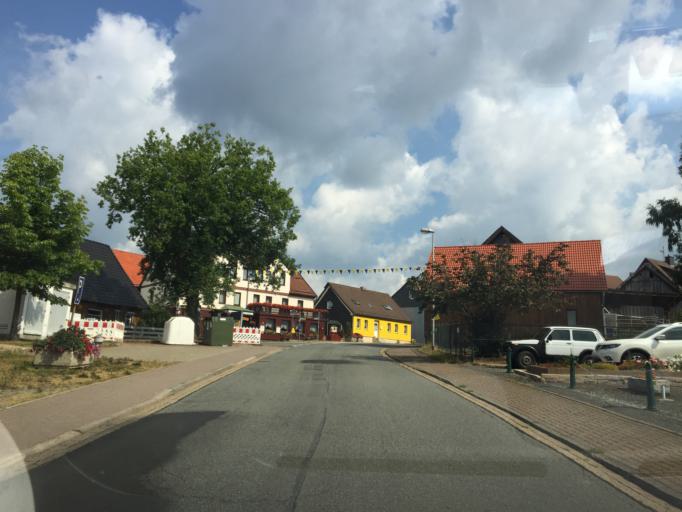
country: DE
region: Lower Saxony
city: Zorge
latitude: 51.6594
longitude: 10.6670
